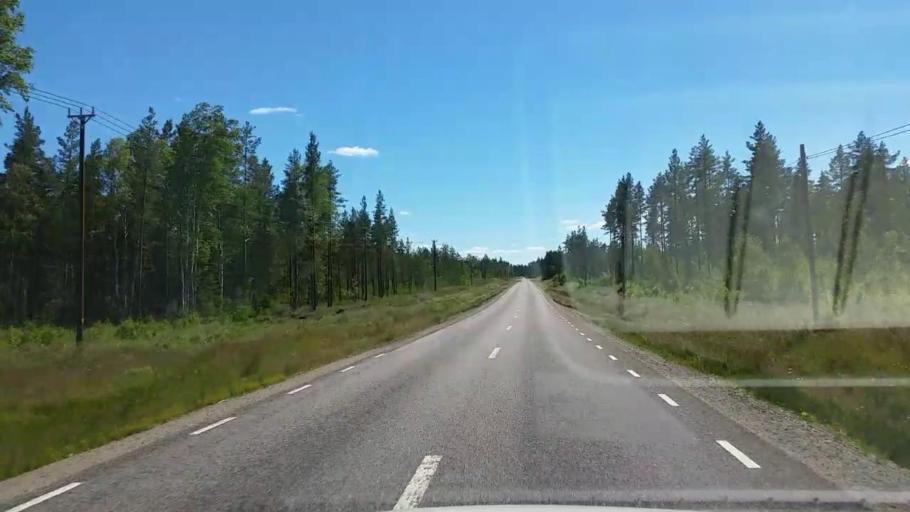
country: SE
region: Gaevleborg
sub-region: Ovanakers Kommun
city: Edsbyn
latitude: 61.4688
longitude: 15.6960
